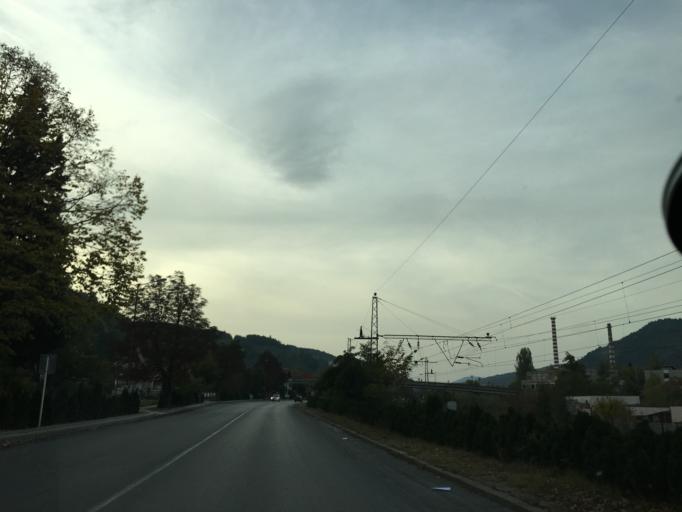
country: BG
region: Pazardzhik
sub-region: Obshtina Belovo
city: Belovo
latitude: 42.2164
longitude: 24.0115
